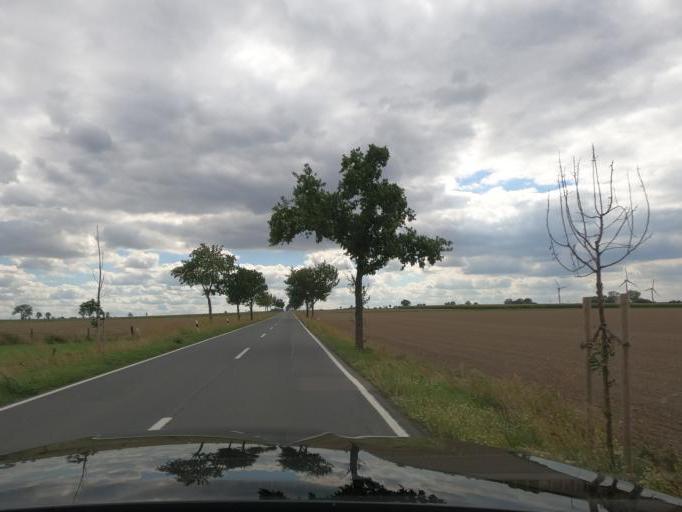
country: DE
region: Lower Saxony
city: Hohenhameln
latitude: 52.2976
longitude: 10.0448
